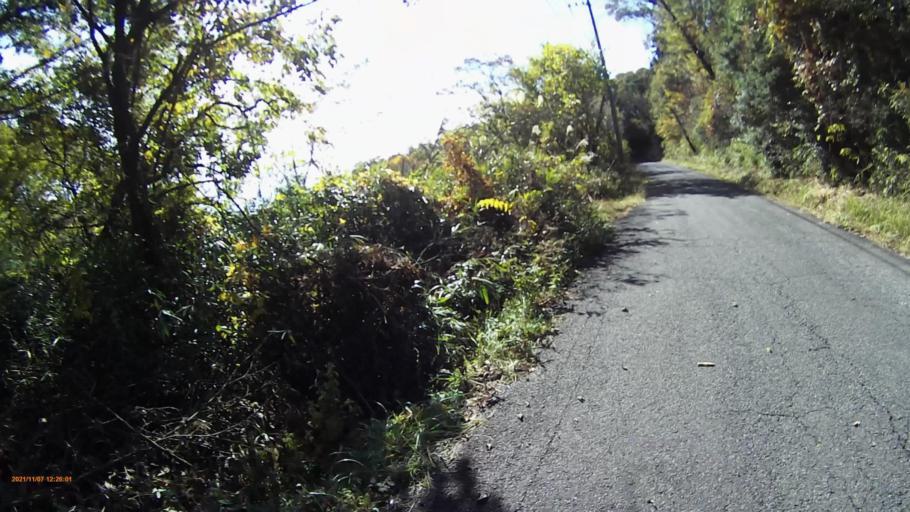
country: JP
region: Gifu
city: Mizunami
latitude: 35.4369
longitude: 137.2606
